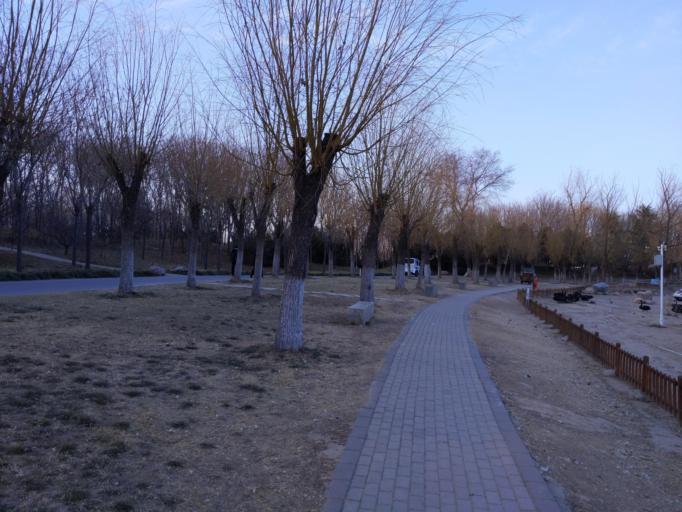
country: CN
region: Henan Sheng
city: Puyang
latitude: 35.7833
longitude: 114.9512
